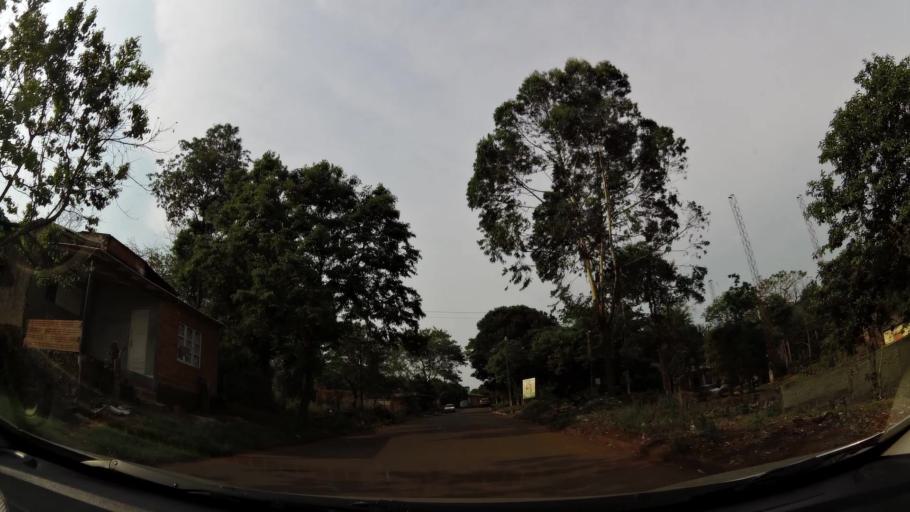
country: PY
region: Alto Parana
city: Ciudad del Este
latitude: -25.4902
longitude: -54.6526
